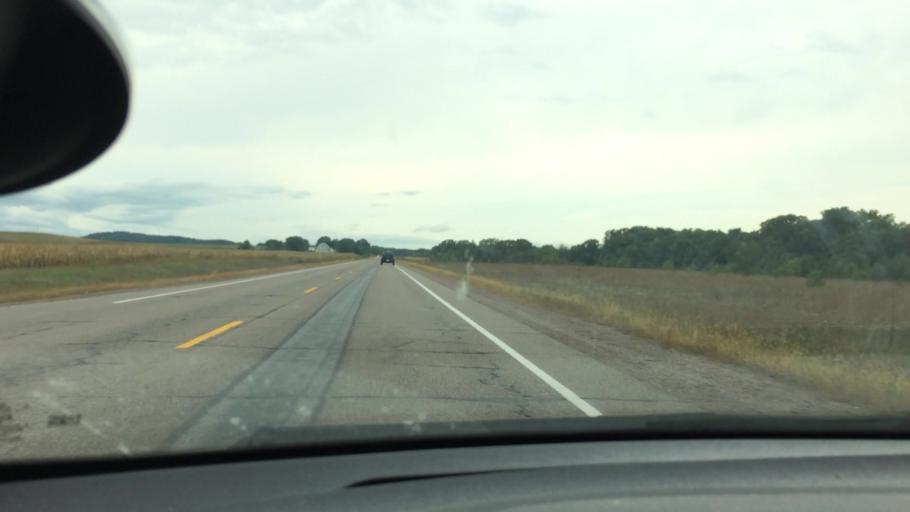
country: US
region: Wisconsin
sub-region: Eau Claire County
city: Augusta
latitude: 44.5859
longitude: -91.1296
